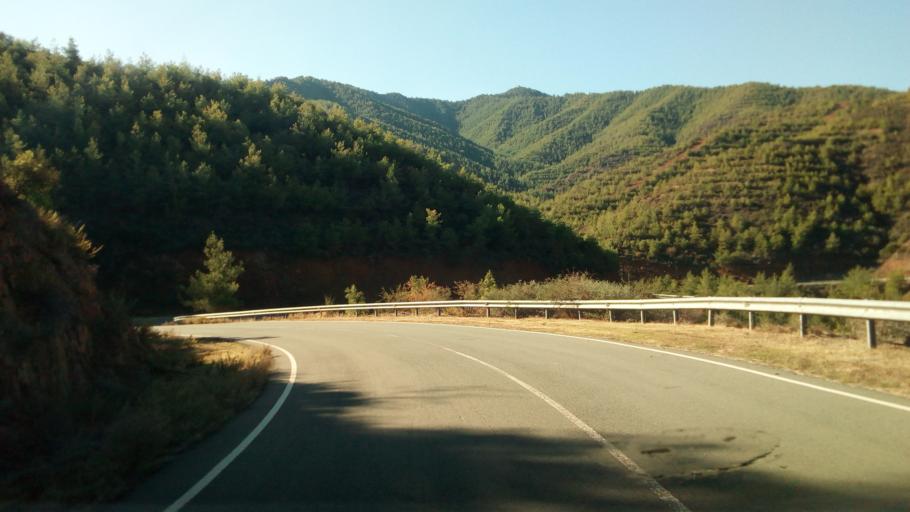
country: CY
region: Lefkosia
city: Kato Pyrgos
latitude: 35.1063
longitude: 32.7479
